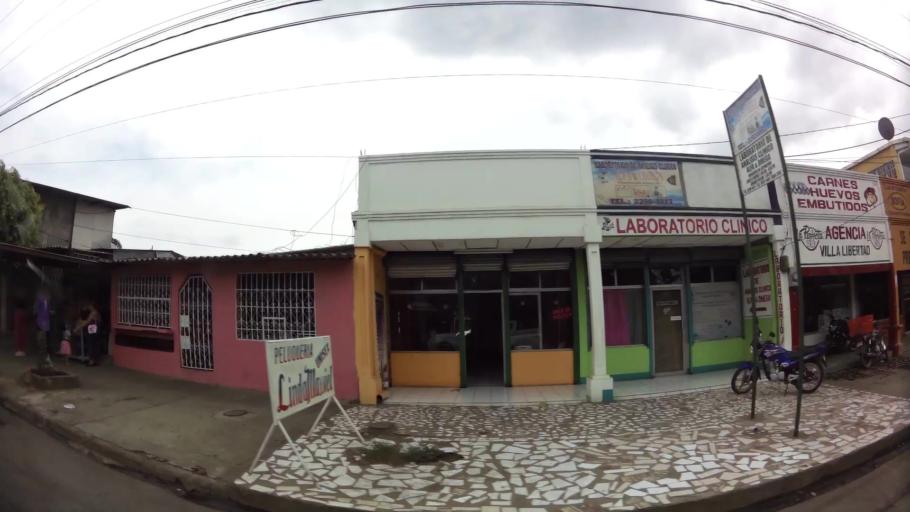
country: NI
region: Managua
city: Managua
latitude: 12.1186
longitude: -86.2036
